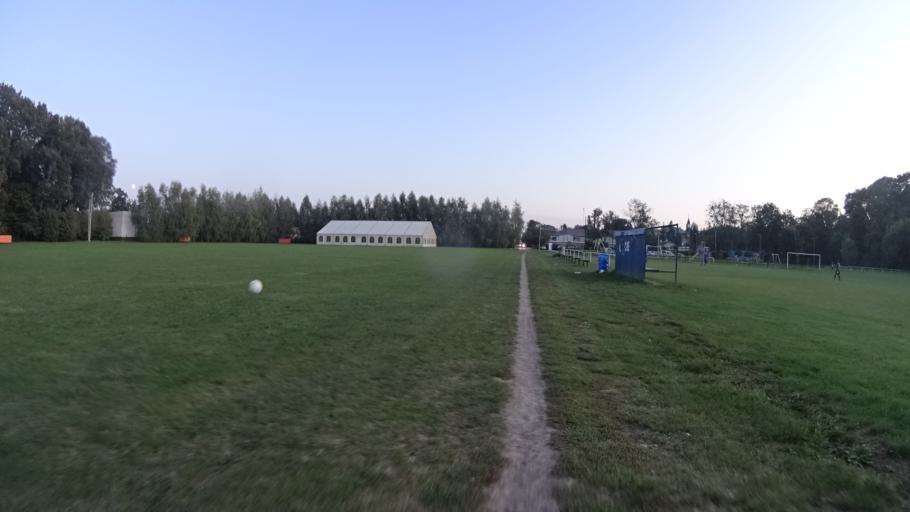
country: PL
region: Masovian Voivodeship
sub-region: Powiat warszawski zachodni
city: Ozarow Mazowiecki
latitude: 52.2160
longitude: 20.7782
